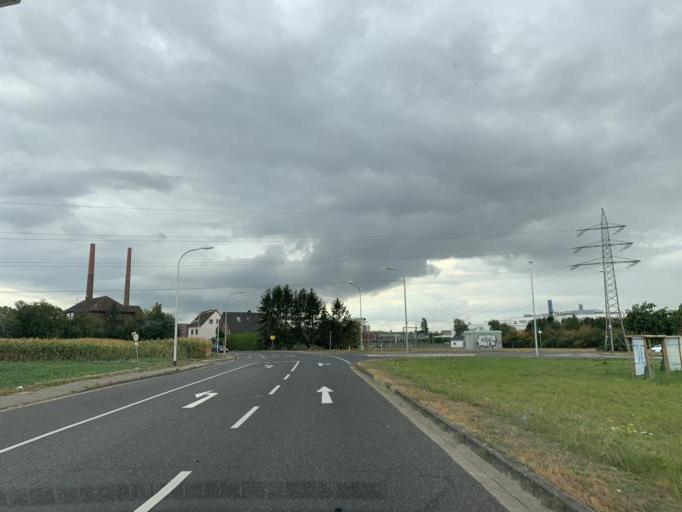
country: DE
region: North Rhine-Westphalia
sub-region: Regierungsbezirk Koln
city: Heinsberg
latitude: 51.0651
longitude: 6.1369
